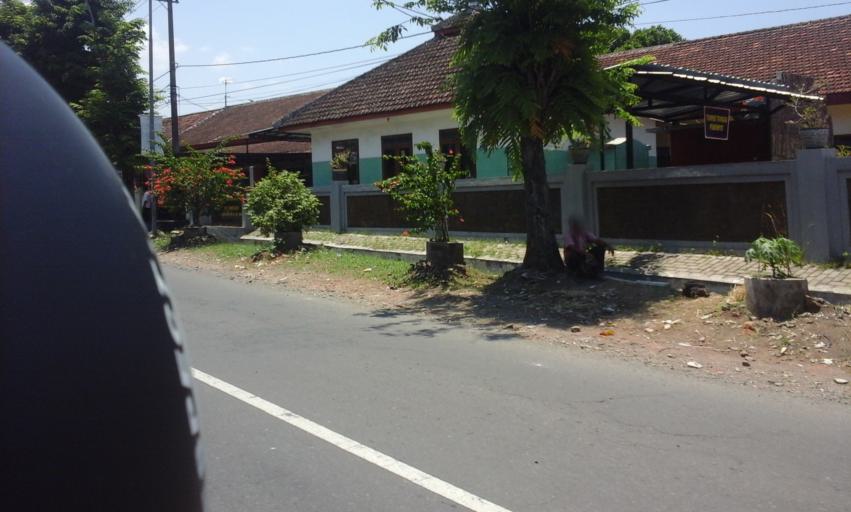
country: ID
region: East Java
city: Sumberdangdang
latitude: -8.1913
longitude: 113.7063
